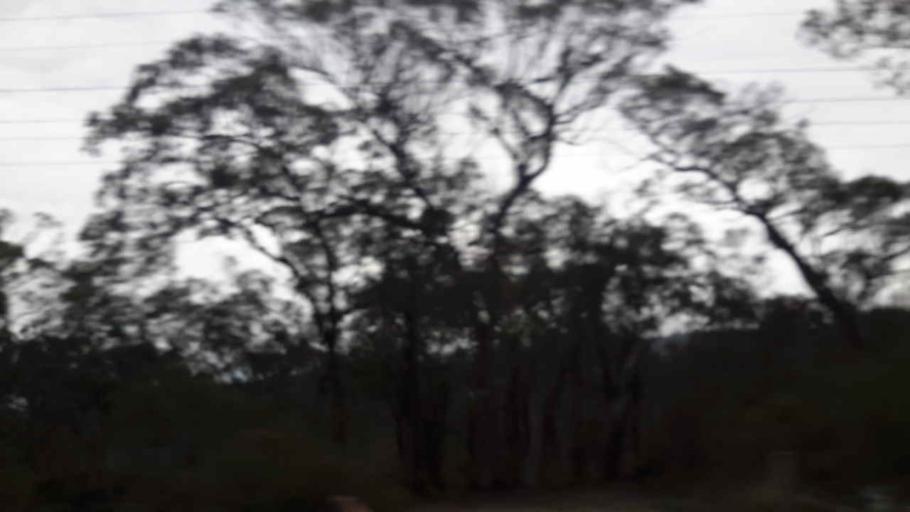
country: AU
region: New South Wales
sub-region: Wollondilly
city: Douglas Park
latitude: -34.1954
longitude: 150.7073
